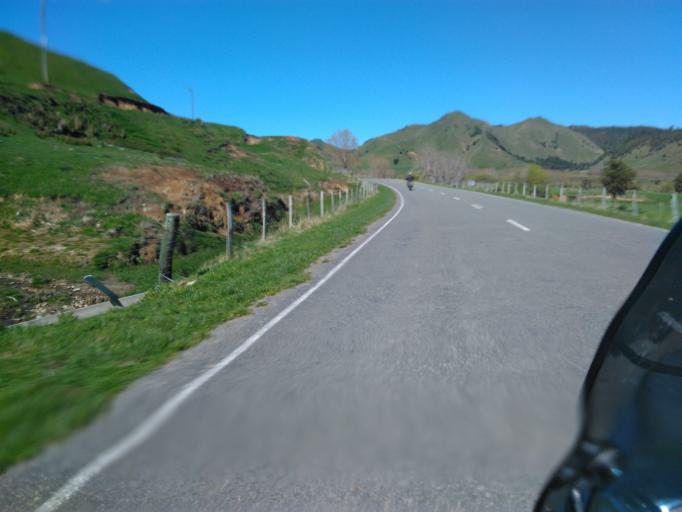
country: NZ
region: Bay of Plenty
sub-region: Opotiki District
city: Opotiki
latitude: -38.3005
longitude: 177.5212
